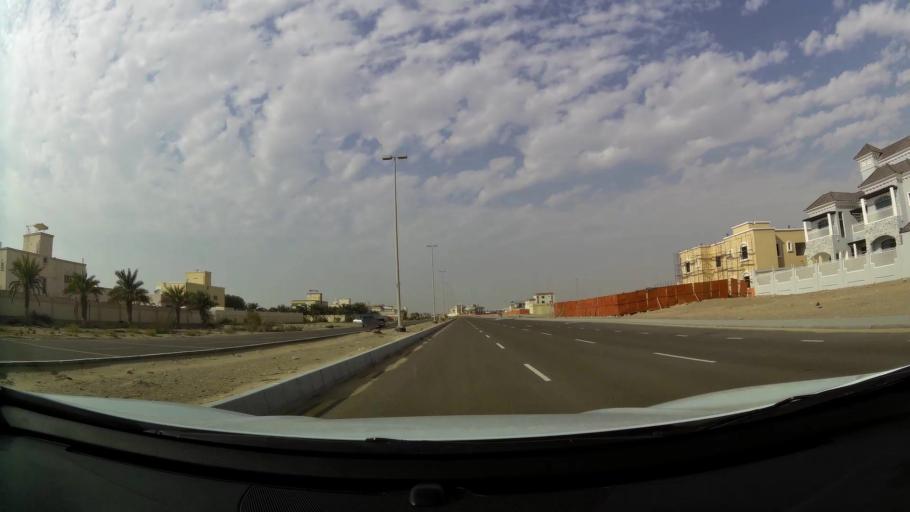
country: AE
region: Abu Dhabi
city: Abu Dhabi
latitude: 24.3291
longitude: 54.5742
